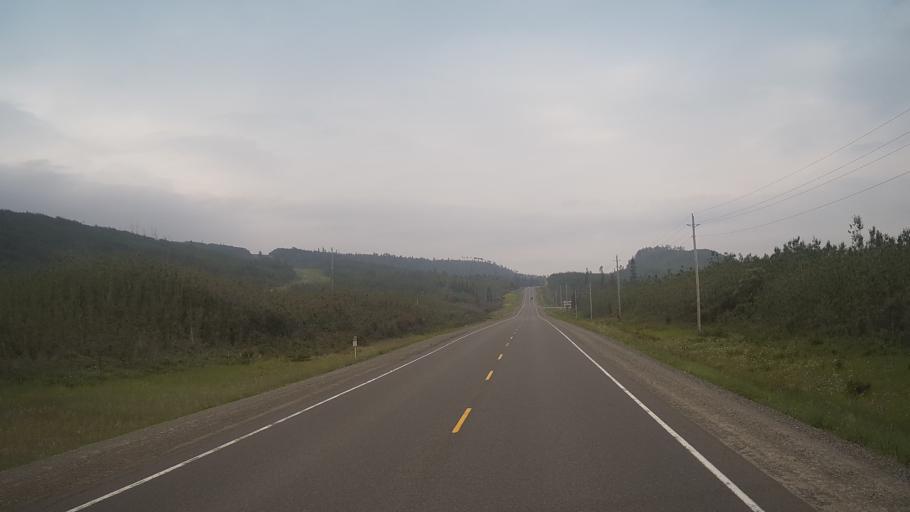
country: CA
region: Ontario
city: Greenstone
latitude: 49.4812
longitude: -88.0890
